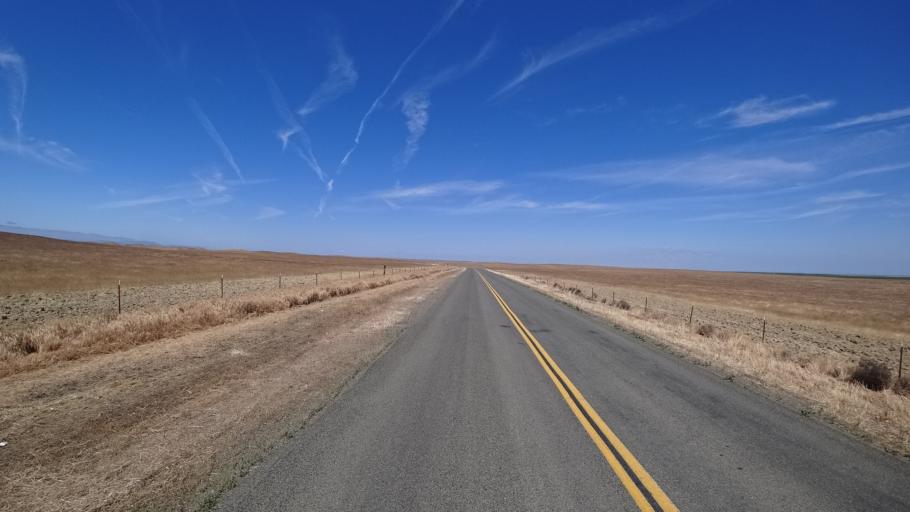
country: US
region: California
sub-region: Kings County
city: Kettleman City
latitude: 35.8074
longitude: -119.8984
